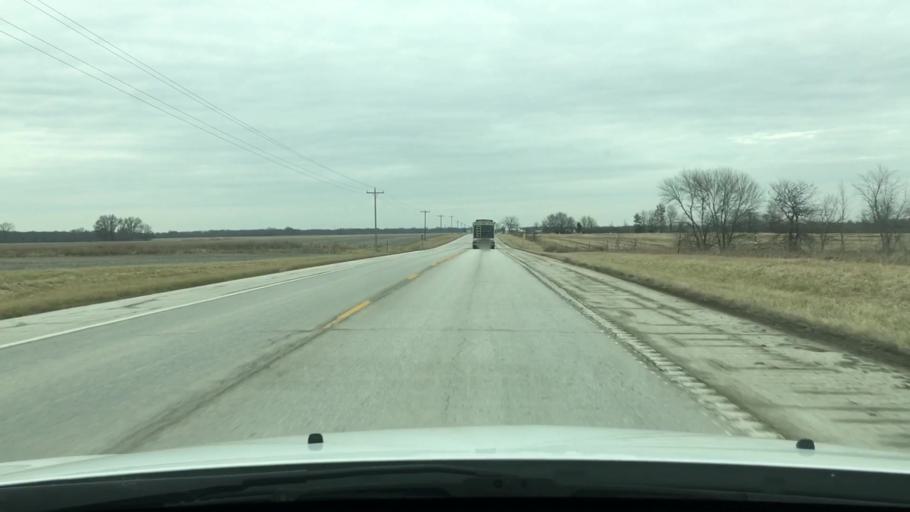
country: US
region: Missouri
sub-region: Montgomery County
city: Wellsville
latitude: 39.1778
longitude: -91.6474
